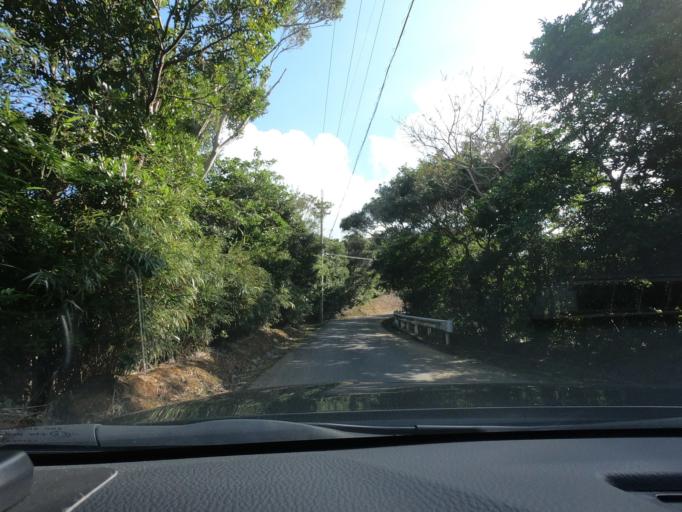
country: JP
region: Okinawa
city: Nago
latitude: 26.7555
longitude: 128.2026
